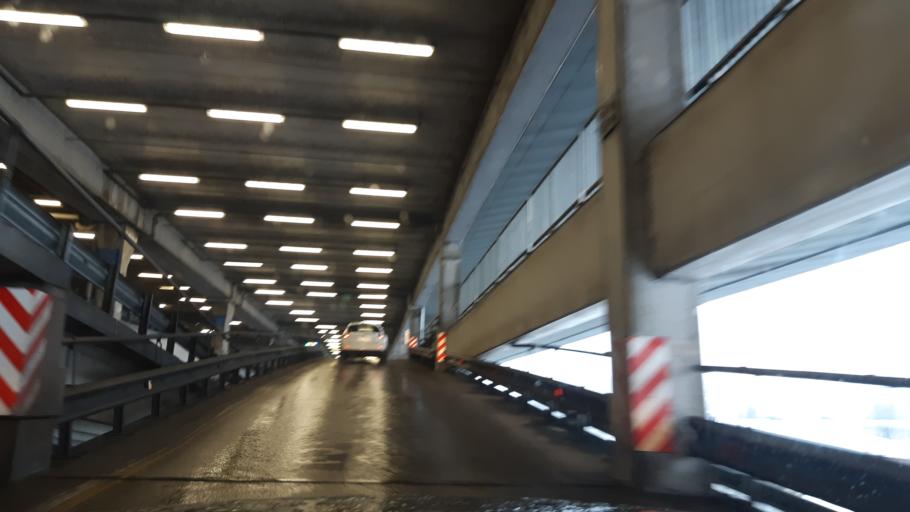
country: LT
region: Kauno apskritis
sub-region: Kaunas
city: Aleksotas
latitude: 54.8909
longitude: 23.9174
